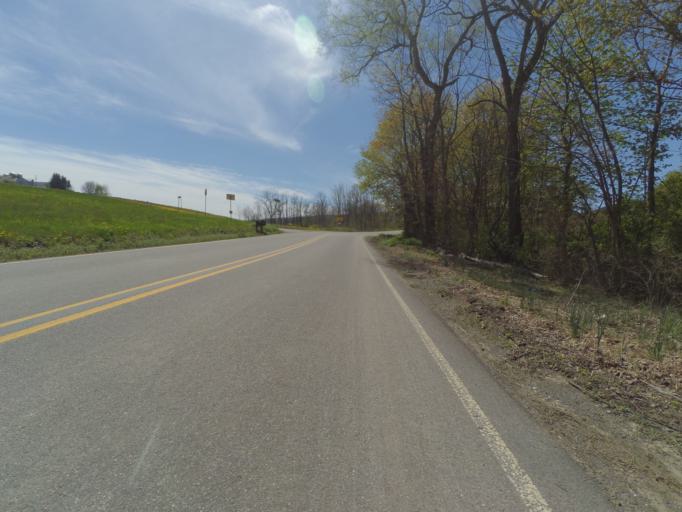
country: US
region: Pennsylvania
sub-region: Blair County
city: Tipton
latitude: 40.6225
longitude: -78.2558
